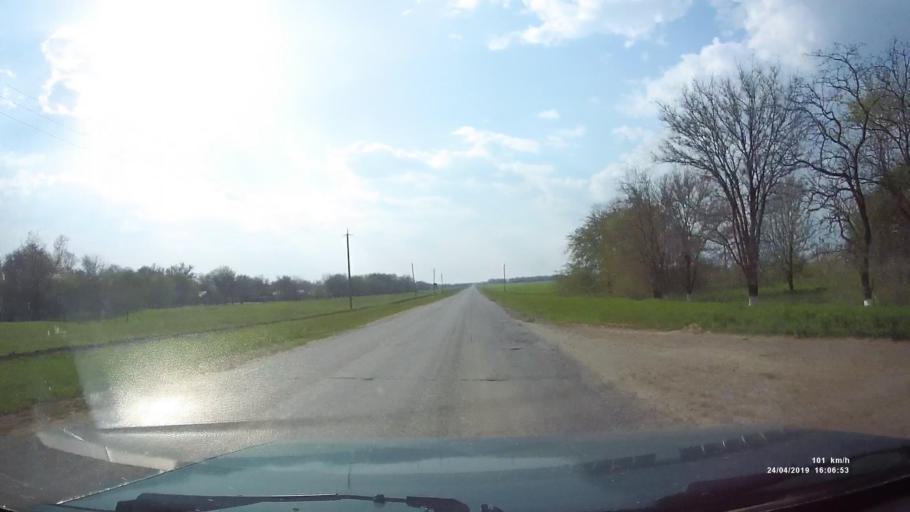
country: RU
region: Rostov
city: Sovetskoye
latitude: 46.6896
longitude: 42.3394
